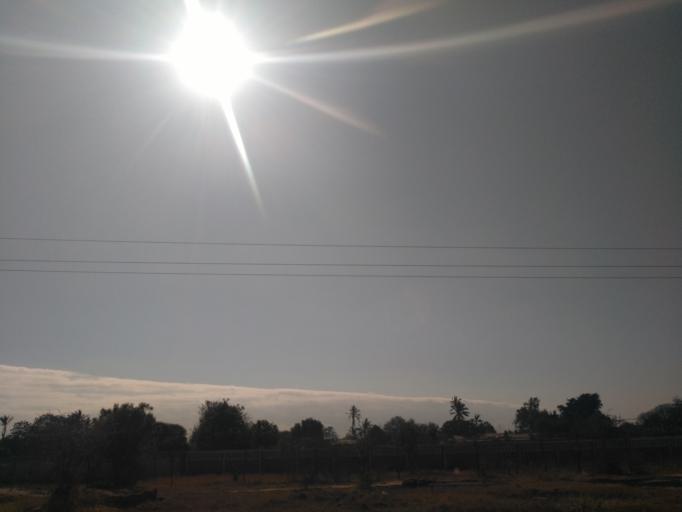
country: TZ
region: Dodoma
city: Dodoma
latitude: -6.1166
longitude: 35.7474
